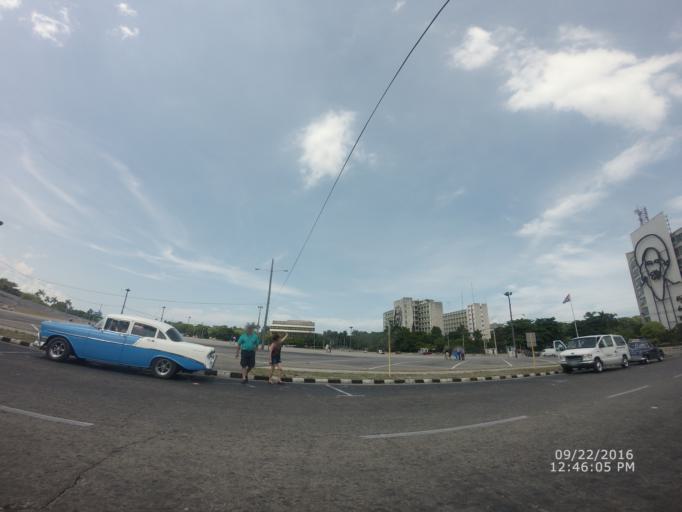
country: CU
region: La Habana
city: Havana
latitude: 23.1241
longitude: -82.3848
